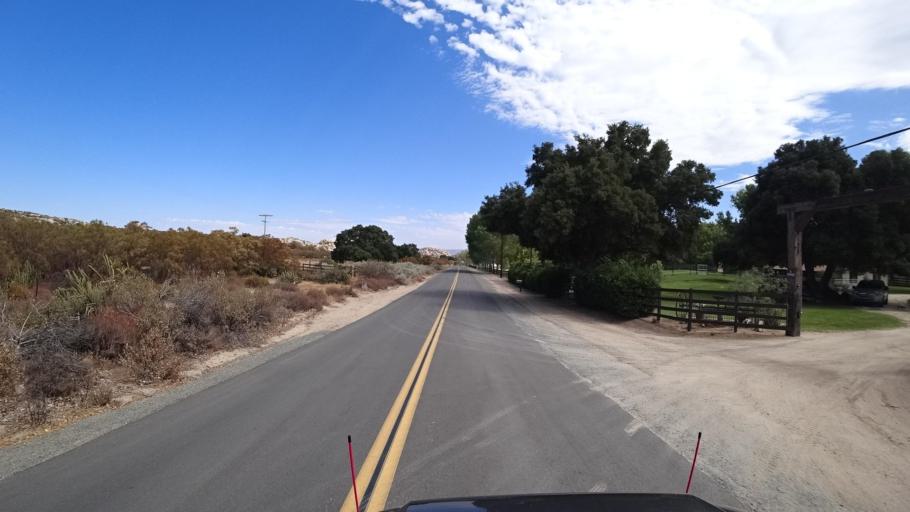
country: MX
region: Baja California
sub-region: Tecate
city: Cereso del Hongo
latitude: 32.6469
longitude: -116.2882
